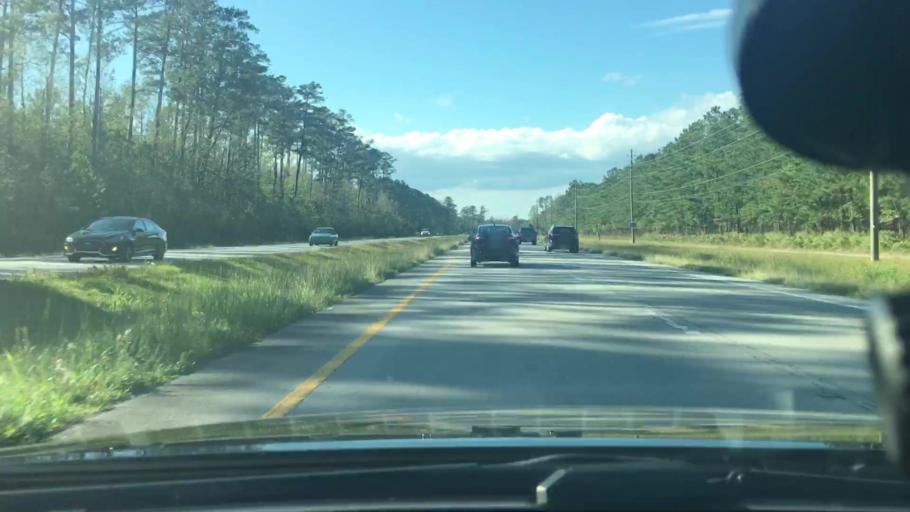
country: US
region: North Carolina
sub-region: Craven County
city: Neuse Forest
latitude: 34.9648
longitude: -76.9602
